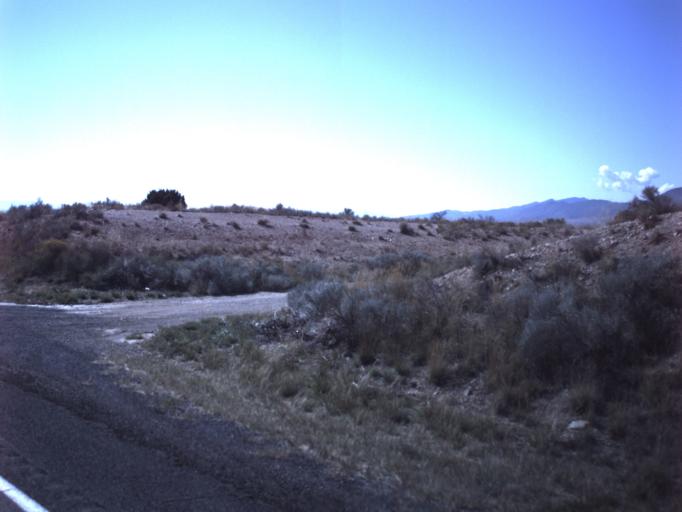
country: US
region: Utah
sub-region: Sanpete County
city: Gunnison
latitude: 39.2793
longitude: -111.8785
